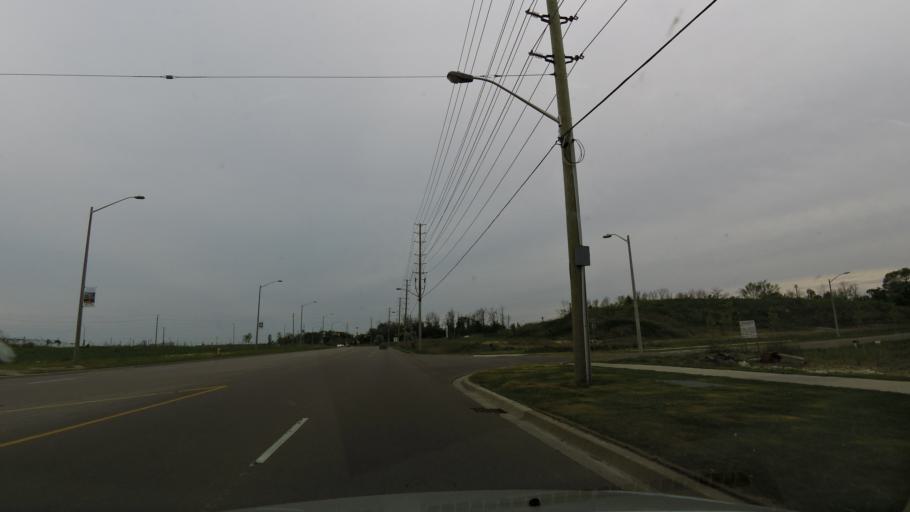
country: CA
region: Ontario
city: Ajax
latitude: 43.8726
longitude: -79.0165
